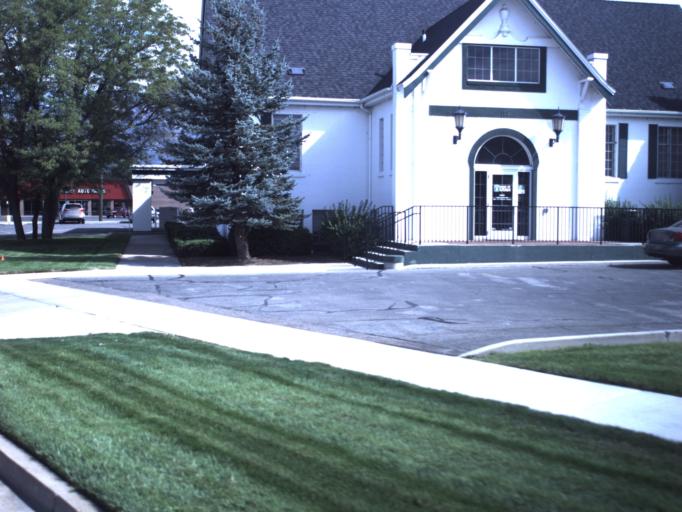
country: US
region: Utah
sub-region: Weber County
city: Harrisville
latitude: 41.2600
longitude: -111.9702
